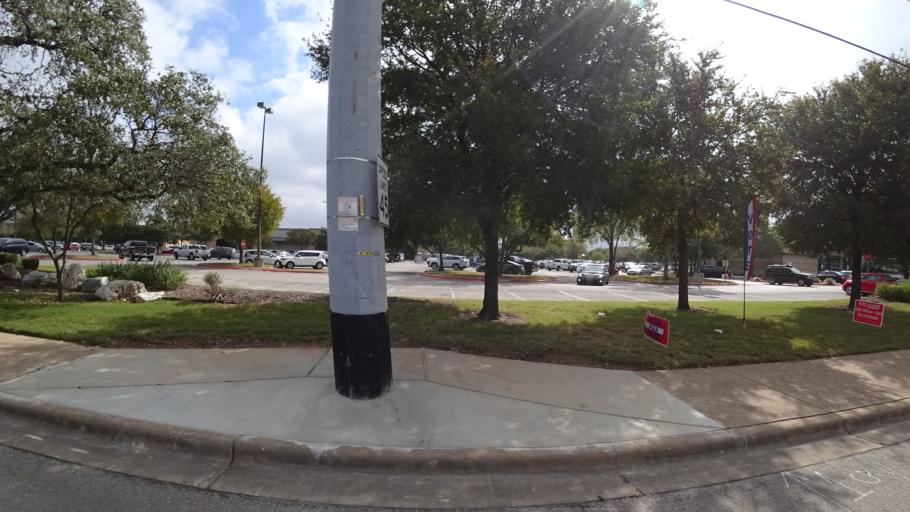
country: US
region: Texas
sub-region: Travis County
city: Shady Hollow
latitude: 30.1843
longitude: -97.8493
